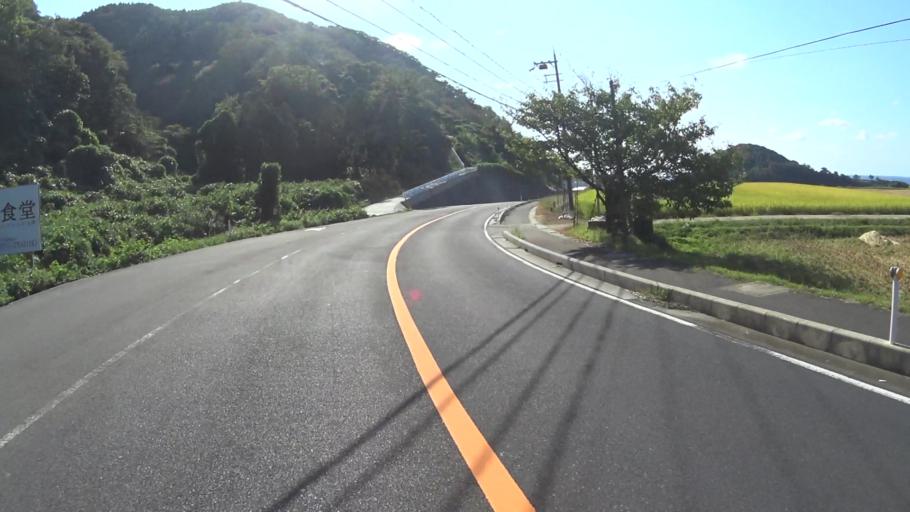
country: JP
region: Kyoto
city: Miyazu
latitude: 35.7418
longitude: 135.1172
